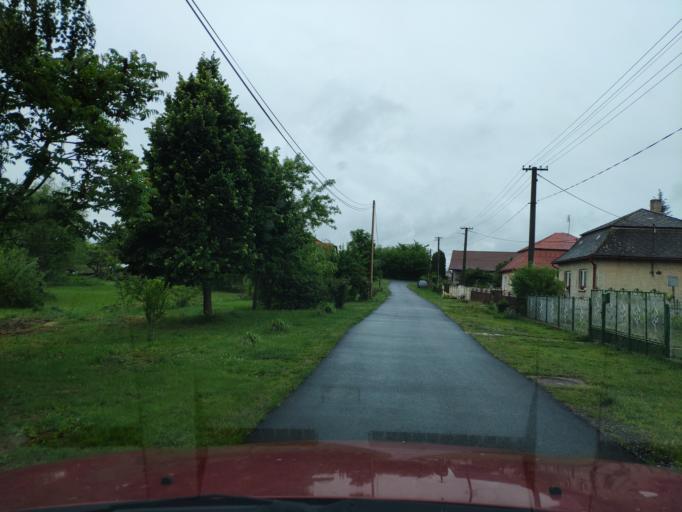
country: SK
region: Kosicky
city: Cierna nad Tisou
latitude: 48.4082
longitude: 22.0627
